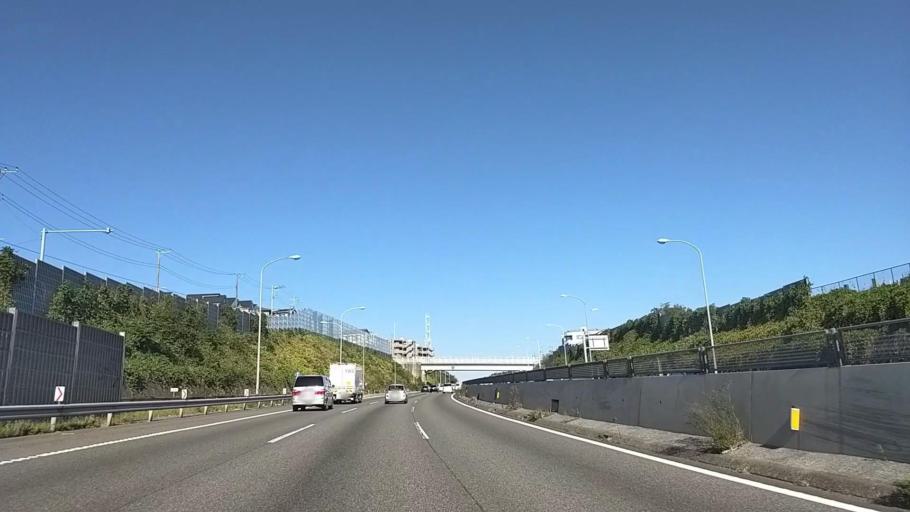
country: JP
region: Kanagawa
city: Minami-rinkan
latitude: 35.4681
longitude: 139.5342
